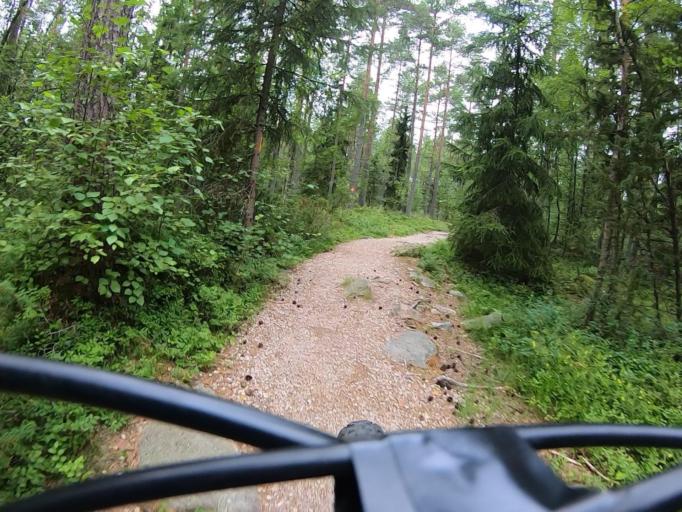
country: FI
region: Varsinais-Suomi
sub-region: Vakka-Suomi
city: Uusikaupunki
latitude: 60.8222
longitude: 21.4136
